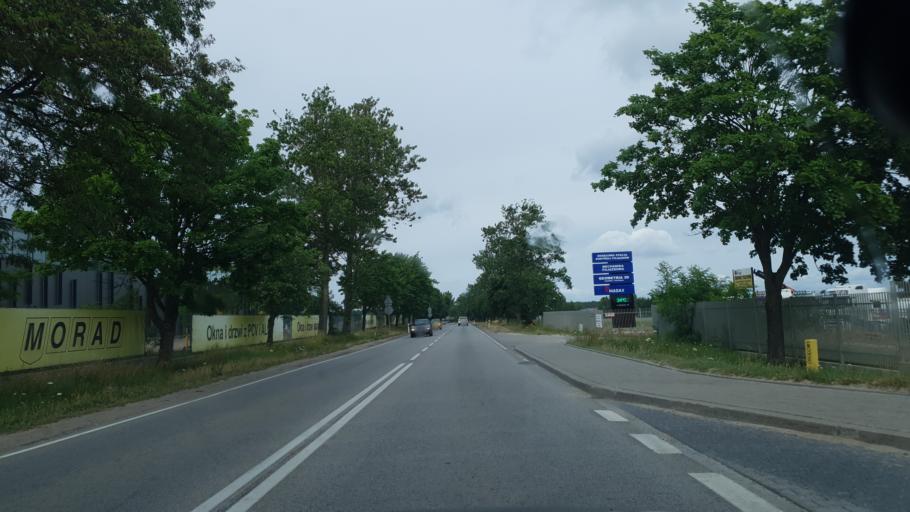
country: PL
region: Pomeranian Voivodeship
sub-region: Powiat kartuski
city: Banino
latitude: 54.4224
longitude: 18.3825
